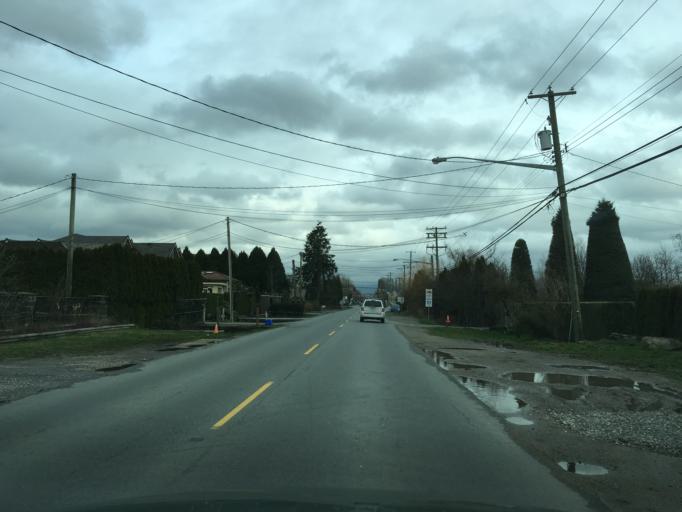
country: CA
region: British Columbia
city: Richmond
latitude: 49.1680
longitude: -123.0692
